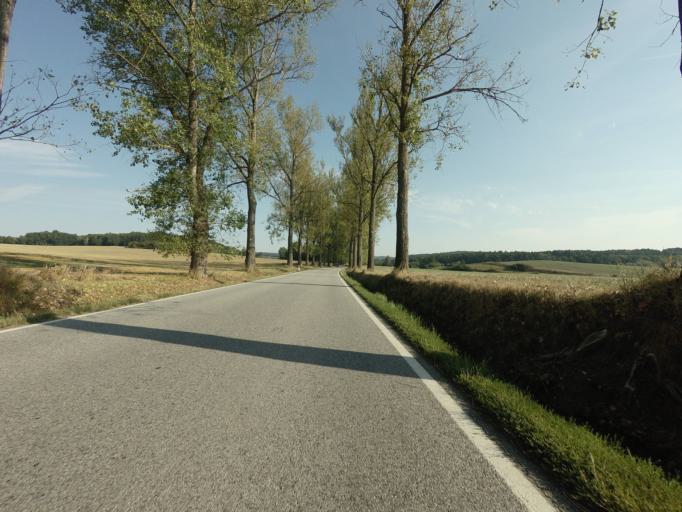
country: CZ
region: Jihocesky
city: Tyn nad Vltavou
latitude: 49.2356
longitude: 14.4207
